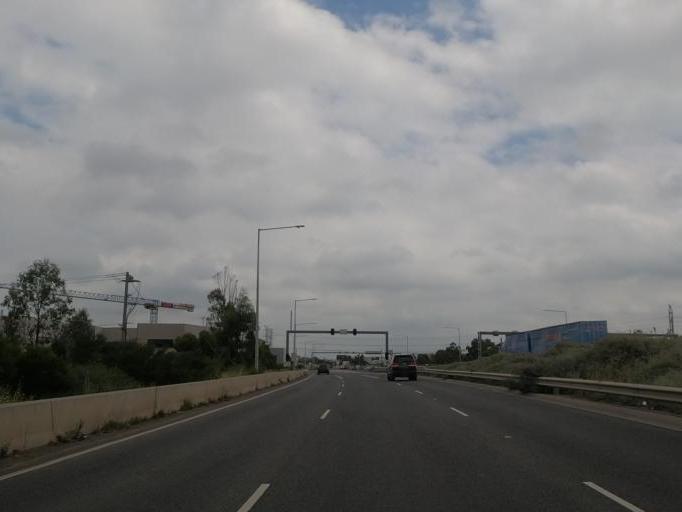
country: AU
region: Victoria
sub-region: Whittlesea
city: Thomastown
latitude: -37.6869
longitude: 145.0261
